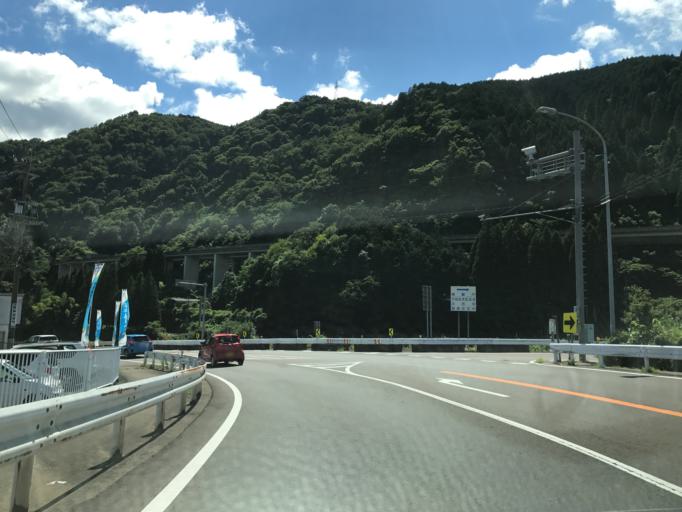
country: JP
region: Gifu
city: Gujo
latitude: 35.7437
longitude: 136.9470
